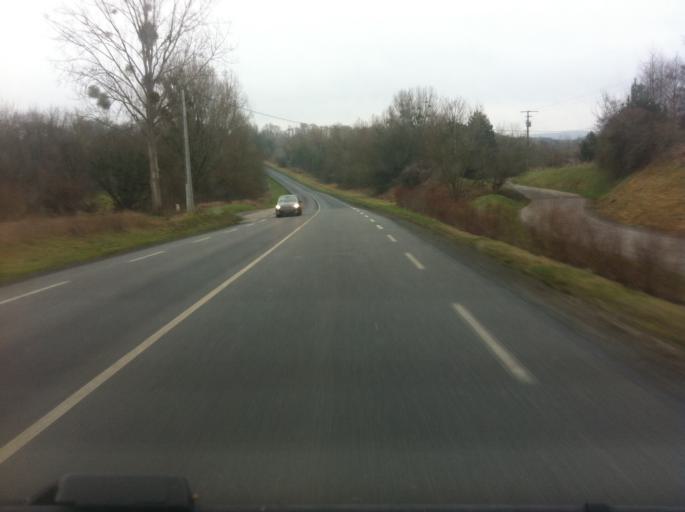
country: FR
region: Haute-Normandie
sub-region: Departement de la Seine-Maritime
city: La Mailleraye-sur-Seine
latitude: 49.4724
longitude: 0.7637
